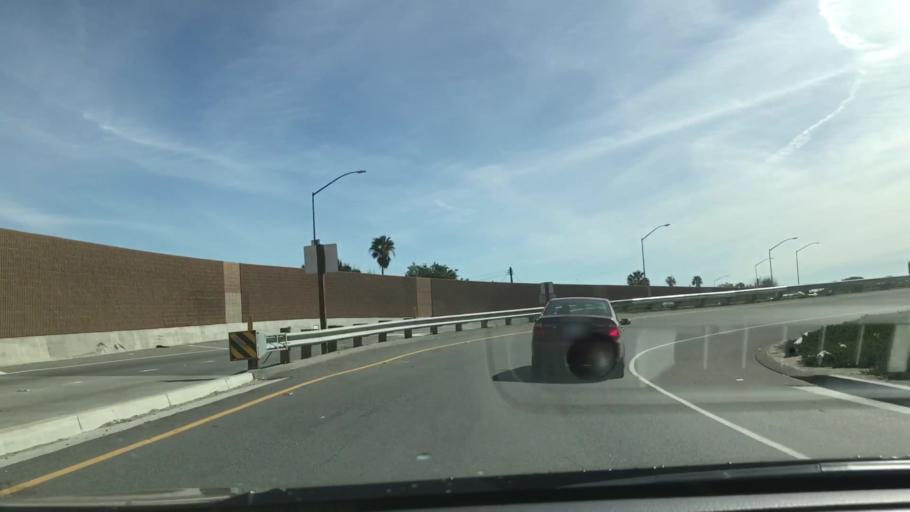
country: US
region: California
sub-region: Los Angeles County
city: San Fernando
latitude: 34.2451
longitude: -118.4213
